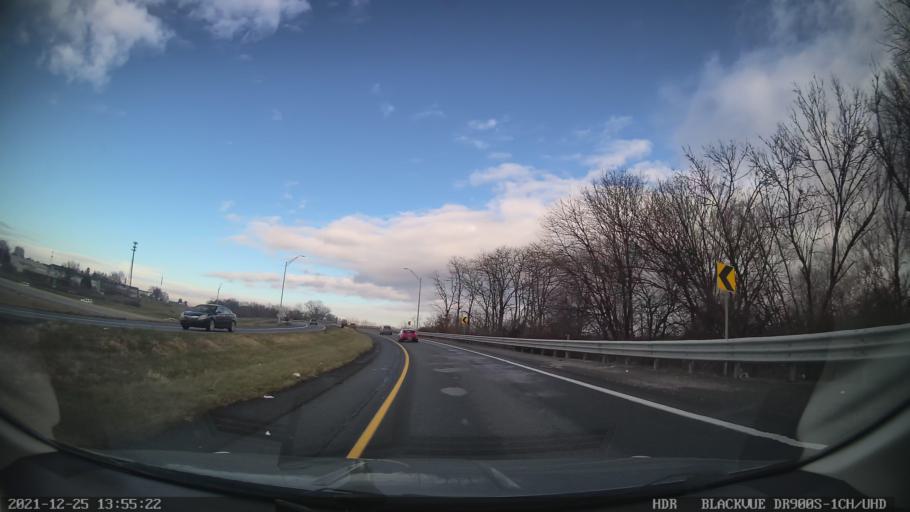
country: US
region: Pennsylvania
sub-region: Lancaster County
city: Lancaster
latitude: 40.0661
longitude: -76.2889
